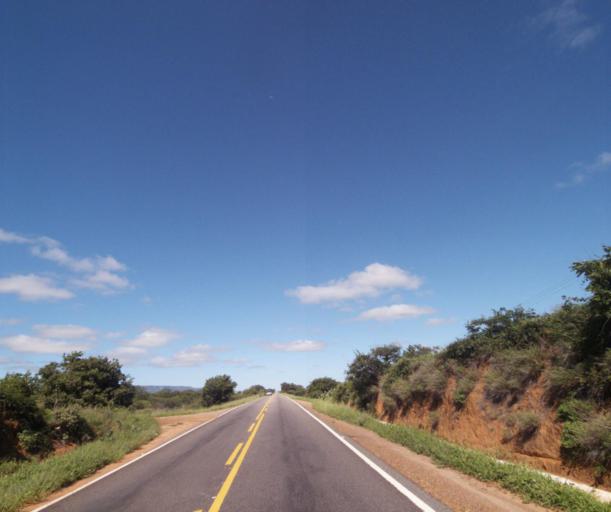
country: BR
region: Bahia
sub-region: Palmas De Monte Alto
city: Palmas de Monte Alto
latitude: -14.2367
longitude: -43.0023
